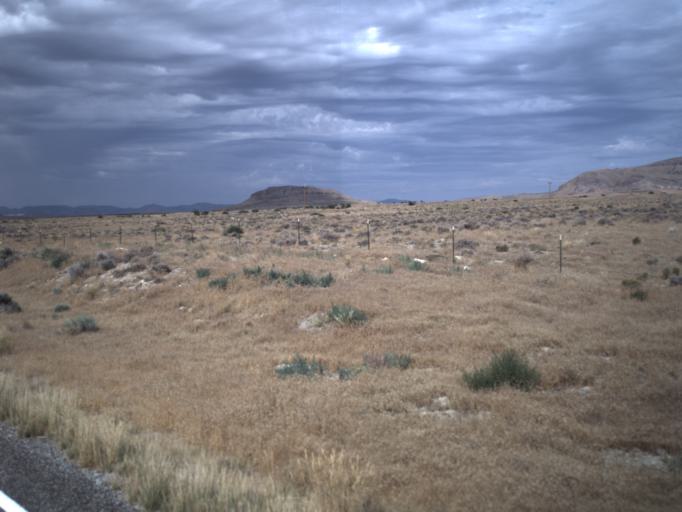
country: US
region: Utah
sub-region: Tooele County
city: Wendover
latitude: 41.4353
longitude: -113.7583
